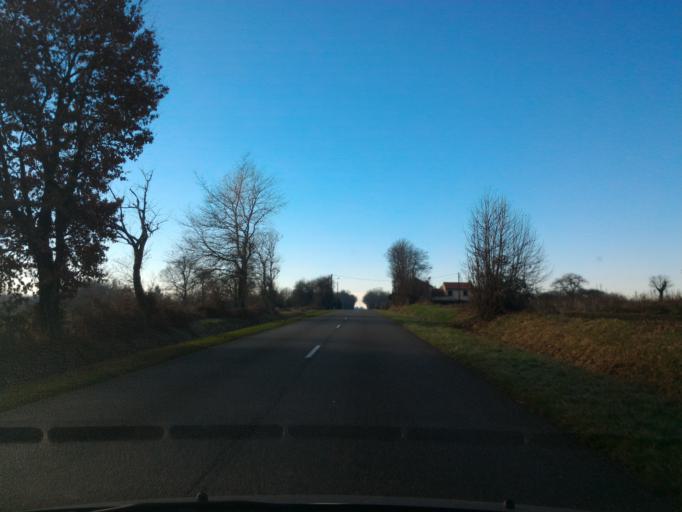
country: FR
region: Poitou-Charentes
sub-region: Departement de la Charente
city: Champagne-Mouton
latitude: 46.0156
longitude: 0.4929
